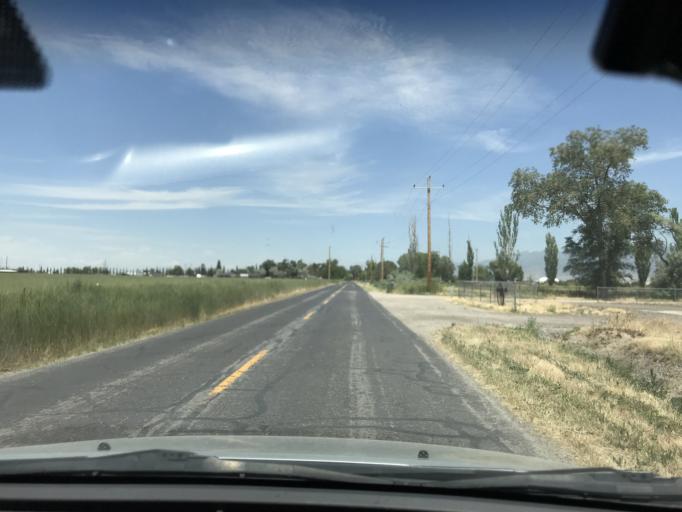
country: US
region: Utah
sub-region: Davis County
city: North Salt Lake
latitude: 40.8307
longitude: -111.9535
